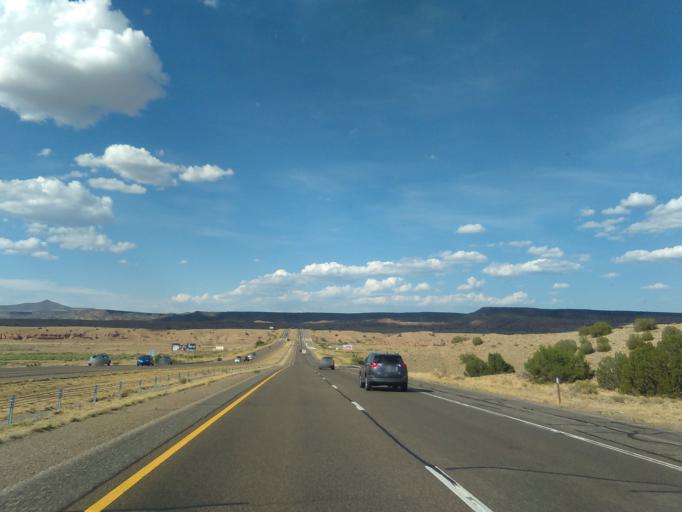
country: US
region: New Mexico
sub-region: Sandoval County
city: Santo Domingo Pueblo
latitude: 35.4936
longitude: -106.2572
